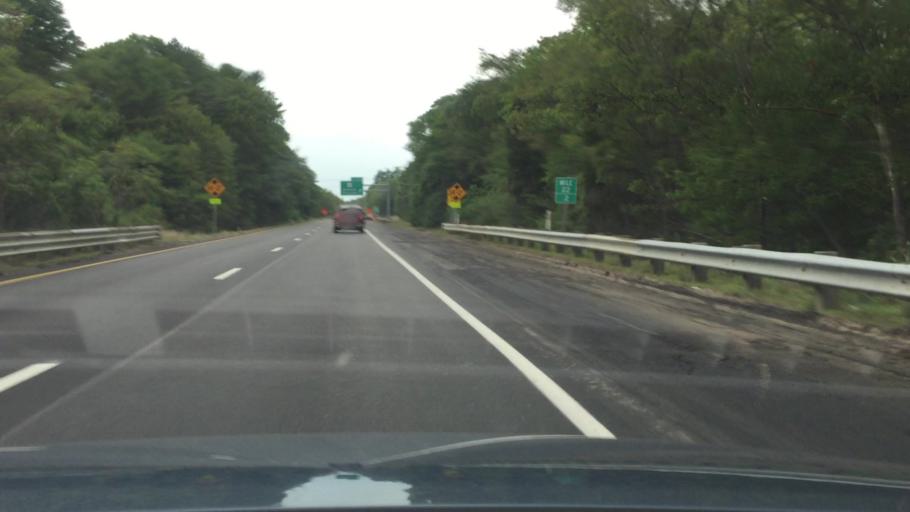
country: US
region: Massachusetts
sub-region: Plymouth County
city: Marshfield
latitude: 42.0508
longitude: -70.7237
